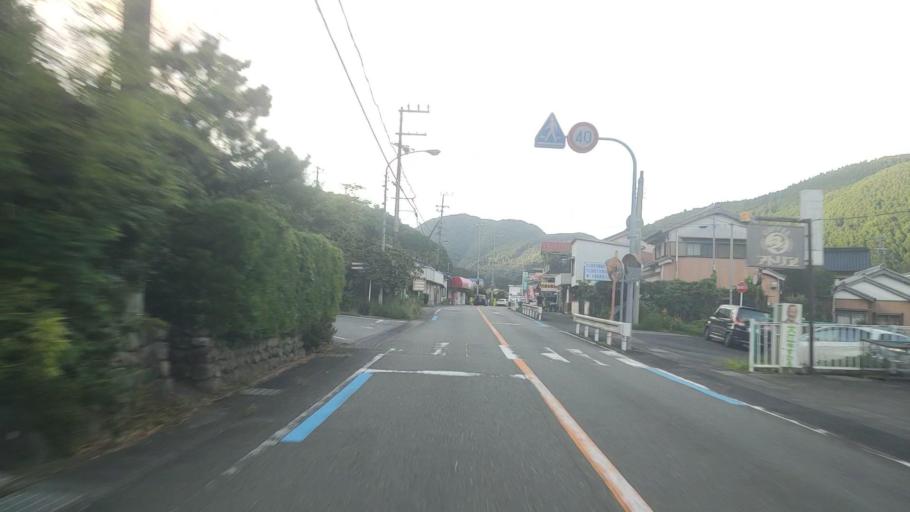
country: JP
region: Wakayama
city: Tanabe
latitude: 33.7913
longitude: 135.5164
